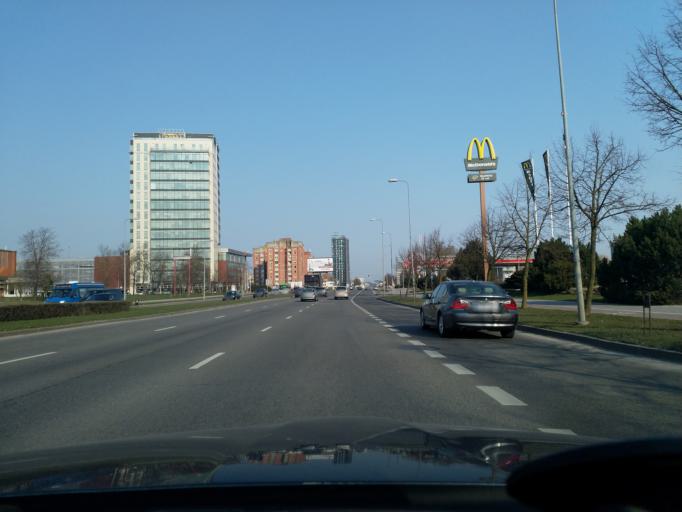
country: LT
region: Klaipedos apskritis
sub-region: Klaipeda
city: Klaipeda
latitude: 55.6913
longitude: 21.1540
